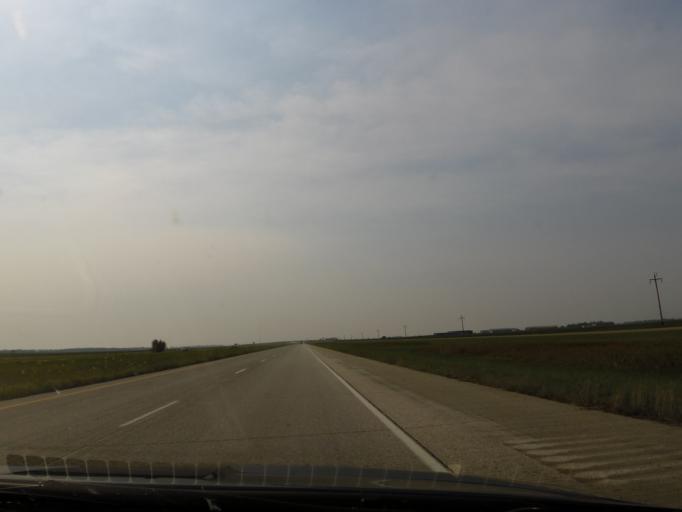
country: US
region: North Dakota
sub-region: Cass County
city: Horace
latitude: 46.7597
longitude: -96.8398
